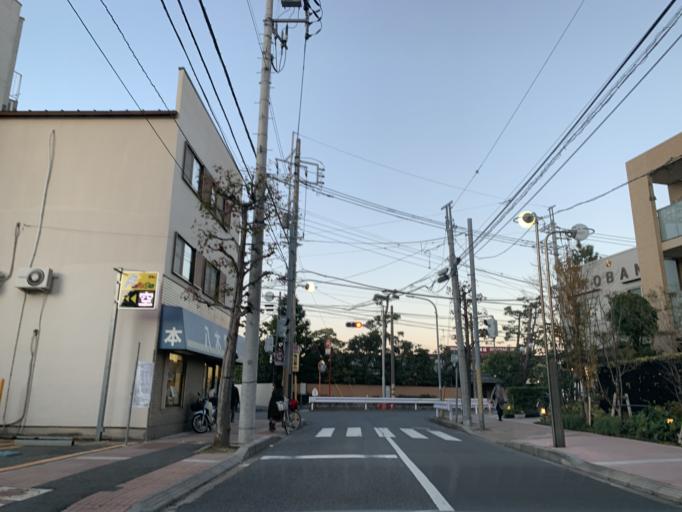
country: JP
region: Chiba
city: Matsudo
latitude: 35.7333
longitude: 139.9113
